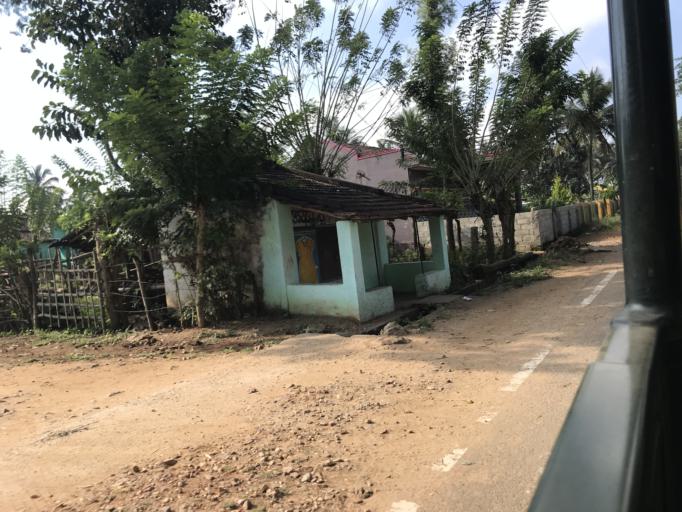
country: IN
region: Karnataka
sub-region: Mysore
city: Heggadadevankote
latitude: 11.9469
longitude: 76.2554
